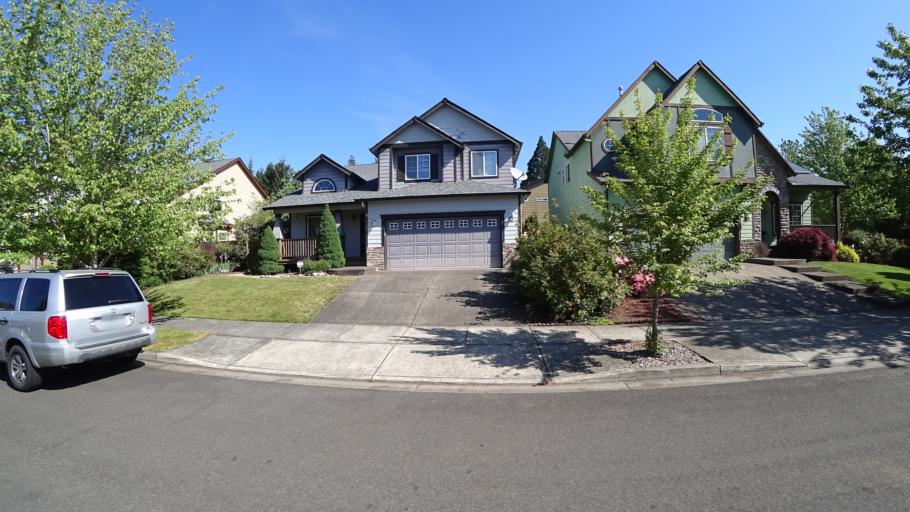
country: US
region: Oregon
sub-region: Washington County
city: Rockcreek
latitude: 45.5225
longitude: -122.9204
